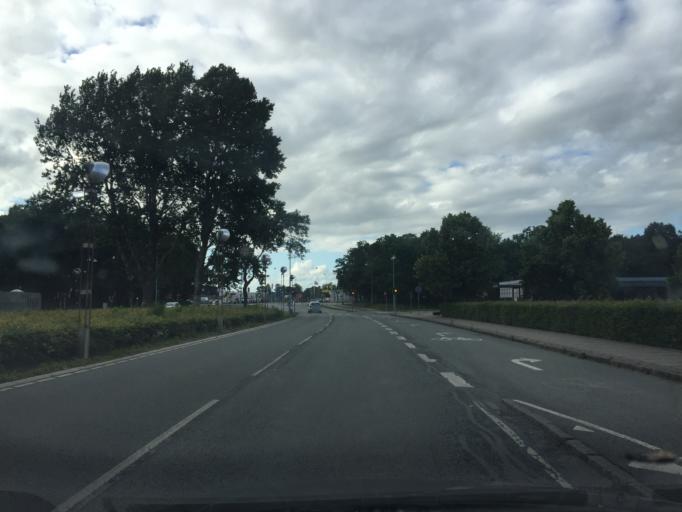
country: DK
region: Capital Region
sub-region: Albertslund Kommune
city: Albertslund
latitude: 55.6616
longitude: 12.3623
